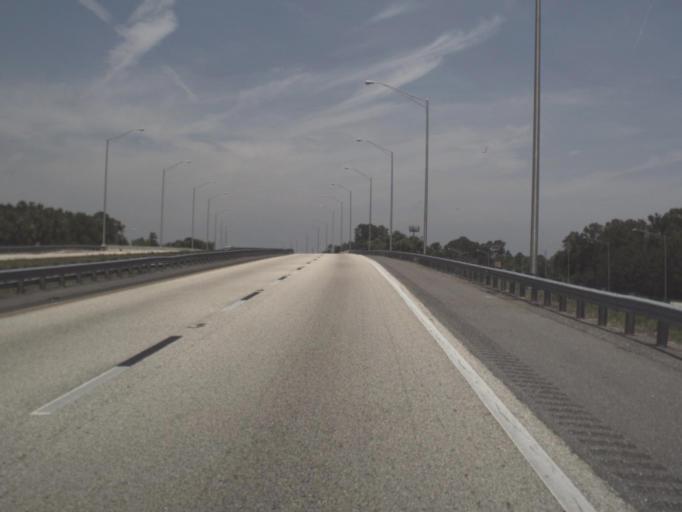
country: US
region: Florida
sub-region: Duval County
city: Atlantic Beach
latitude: 30.3143
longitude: -81.5241
